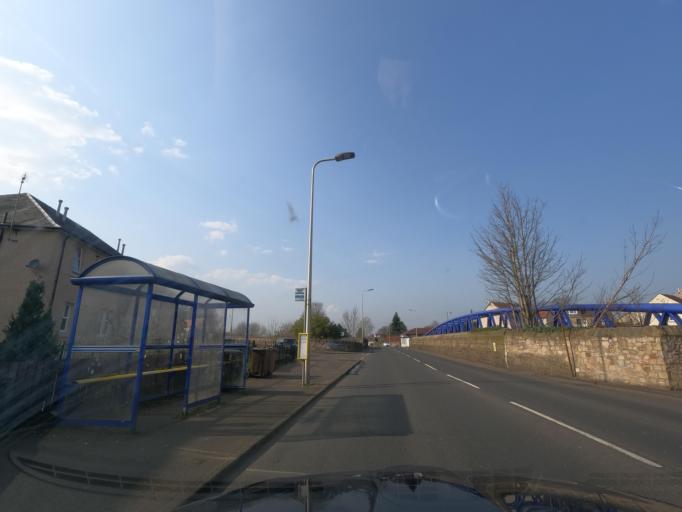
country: GB
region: Scotland
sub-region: Falkirk
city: Grangemouth
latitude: 55.9865
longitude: -3.7377
